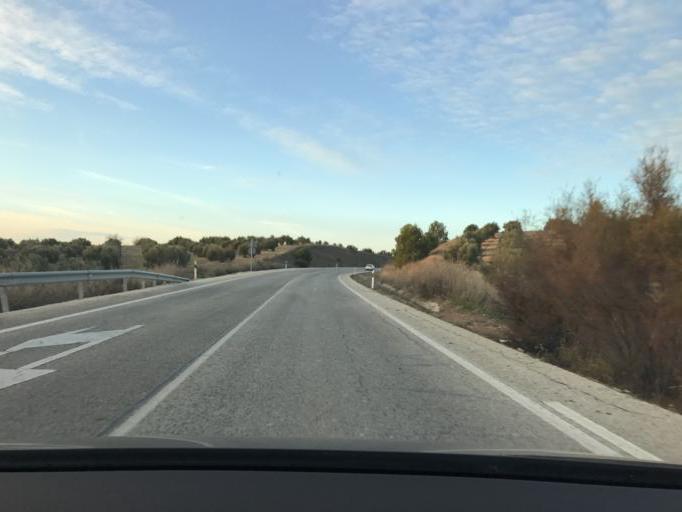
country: ES
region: Andalusia
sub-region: Provincia de Jaen
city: Ubeda
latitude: 37.9289
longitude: -3.3545
